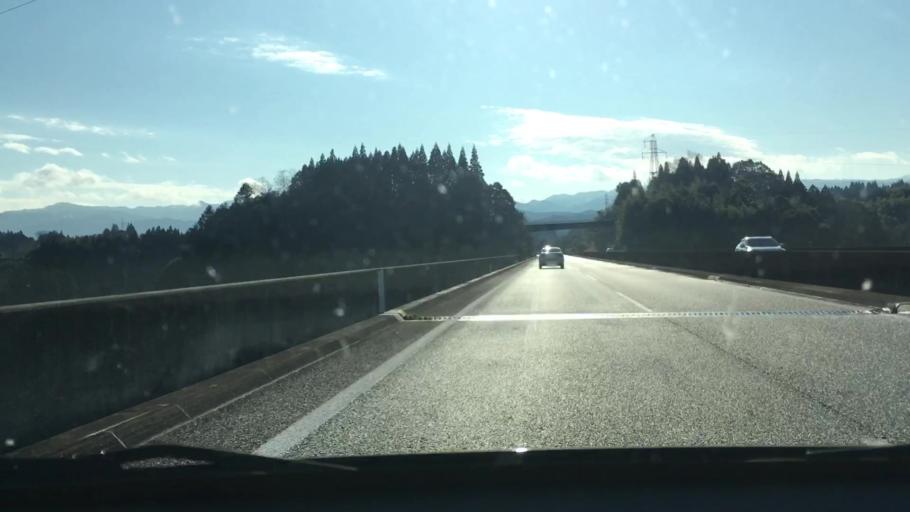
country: JP
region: Kumamoto
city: Hitoyoshi
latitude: 32.2137
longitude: 130.7772
